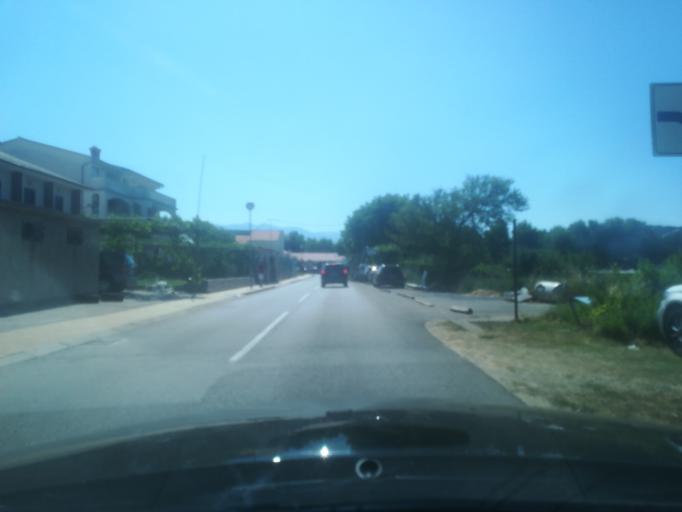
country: HR
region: Primorsko-Goranska
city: Lopar
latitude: 44.8255
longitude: 14.7382
